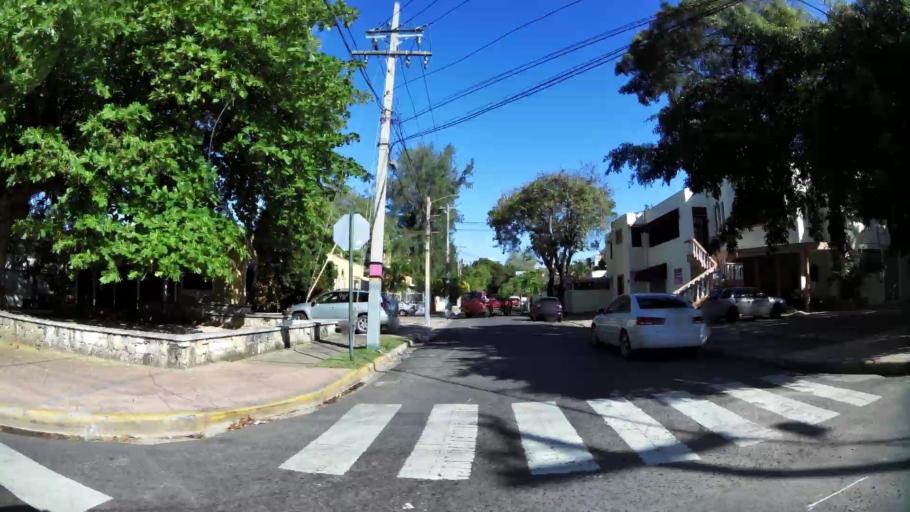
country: DO
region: Nacional
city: Ciudad Nueva
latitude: 18.4618
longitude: -69.9054
